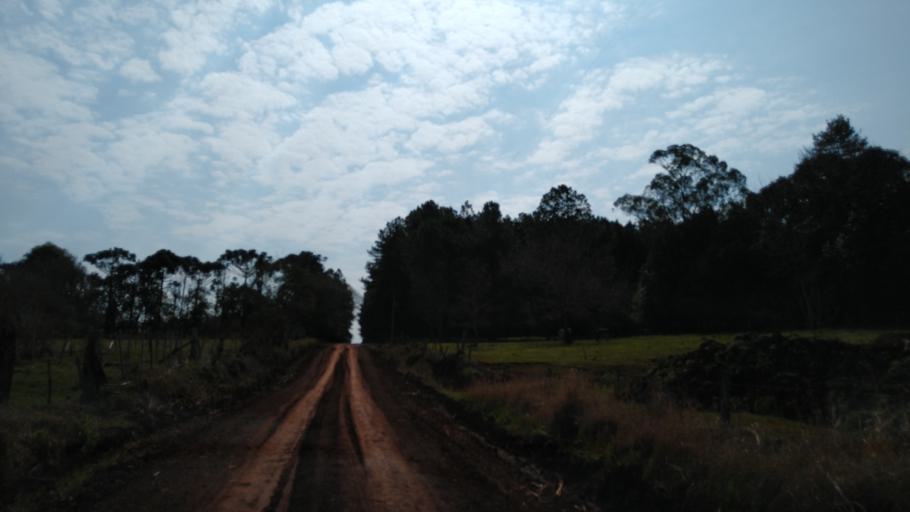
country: AR
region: Misiones
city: Capiovi
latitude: -26.9450
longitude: -55.0436
